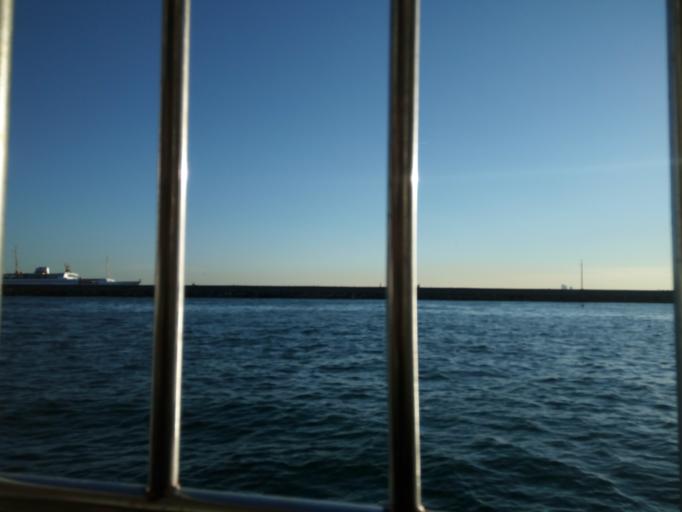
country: TR
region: Istanbul
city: UEskuedar
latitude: 41.0009
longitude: 29.0094
